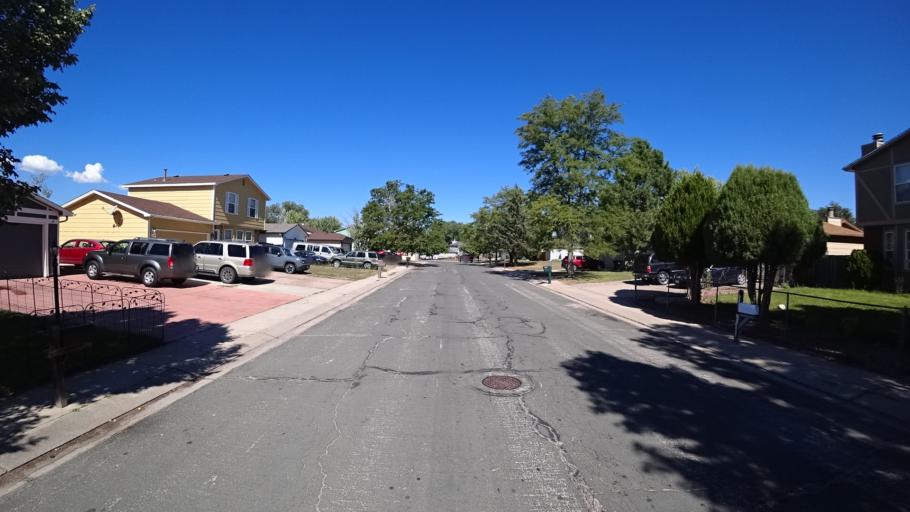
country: US
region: Colorado
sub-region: El Paso County
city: Cimarron Hills
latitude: 38.8165
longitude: -104.7366
